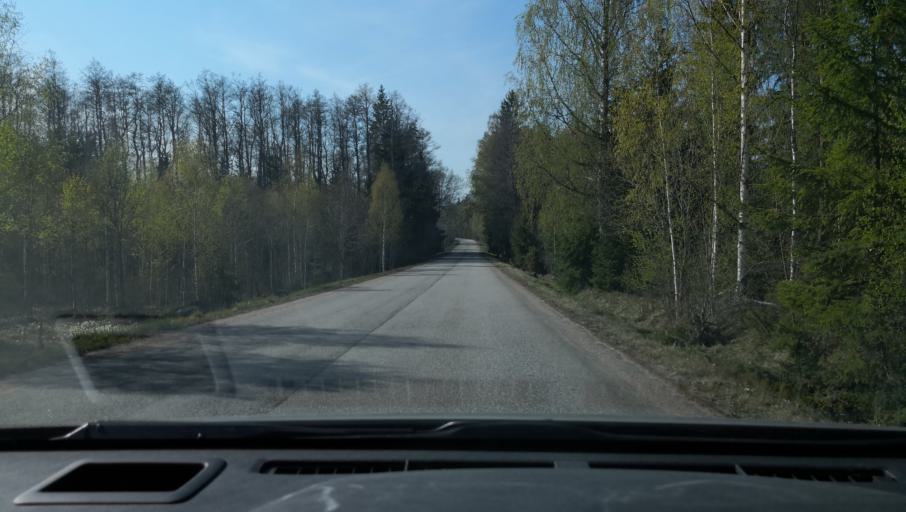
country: SE
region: Uppsala
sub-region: Heby Kommun
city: Tarnsjo
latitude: 60.2634
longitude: 16.9293
